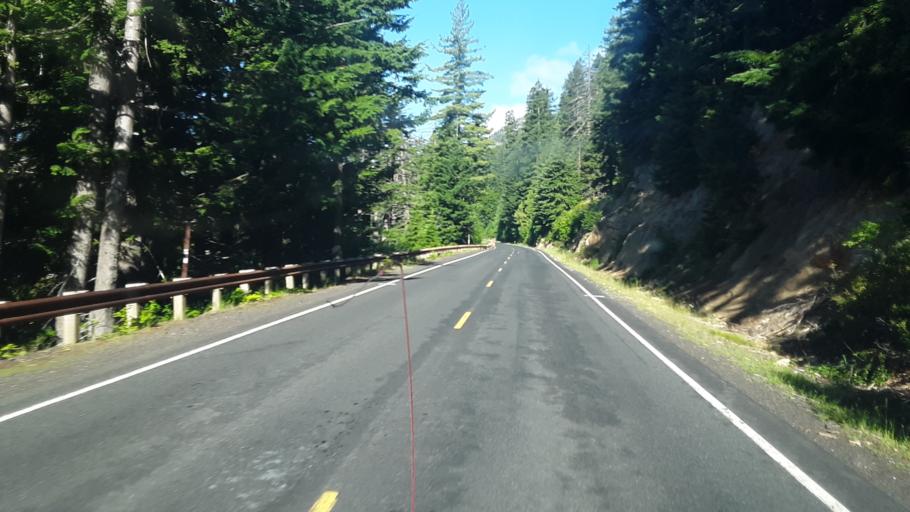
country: US
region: Washington
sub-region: Kittitas County
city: Cle Elum
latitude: 46.8969
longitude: -121.4568
